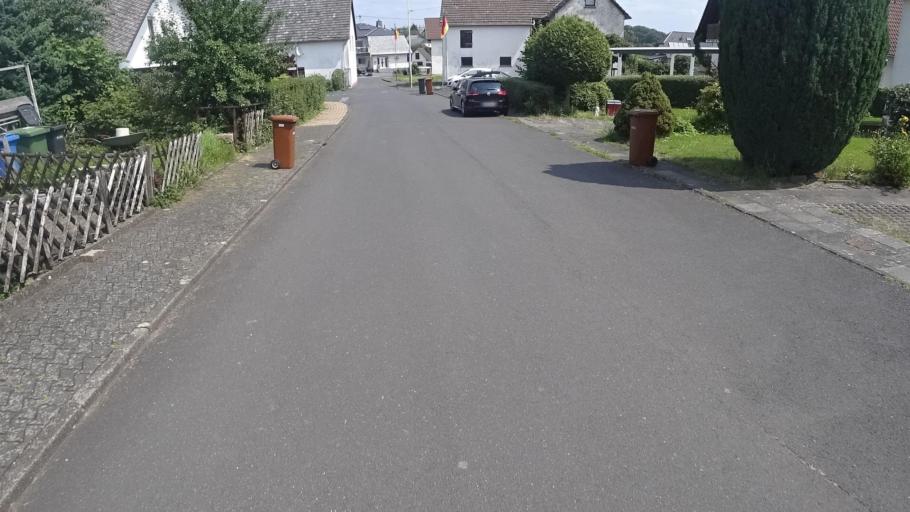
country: DE
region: Rheinland-Pfalz
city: Vettelschoss
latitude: 50.5979
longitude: 7.3616
